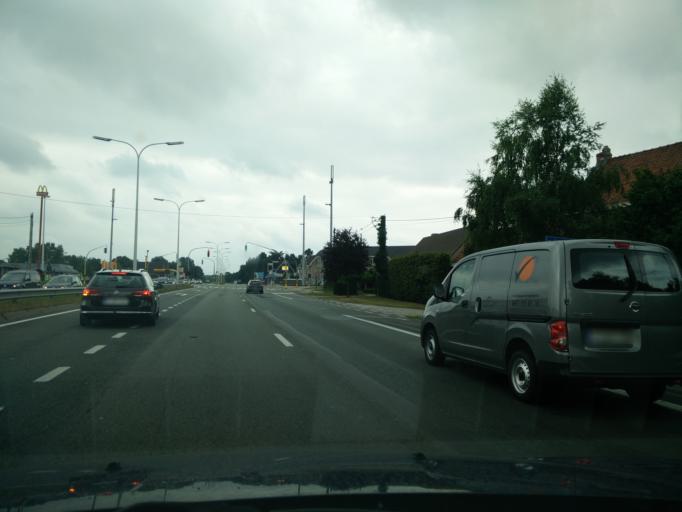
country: BE
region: Flanders
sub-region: Provincie Oost-Vlaanderen
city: Zingem
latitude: 50.9105
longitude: 3.6173
